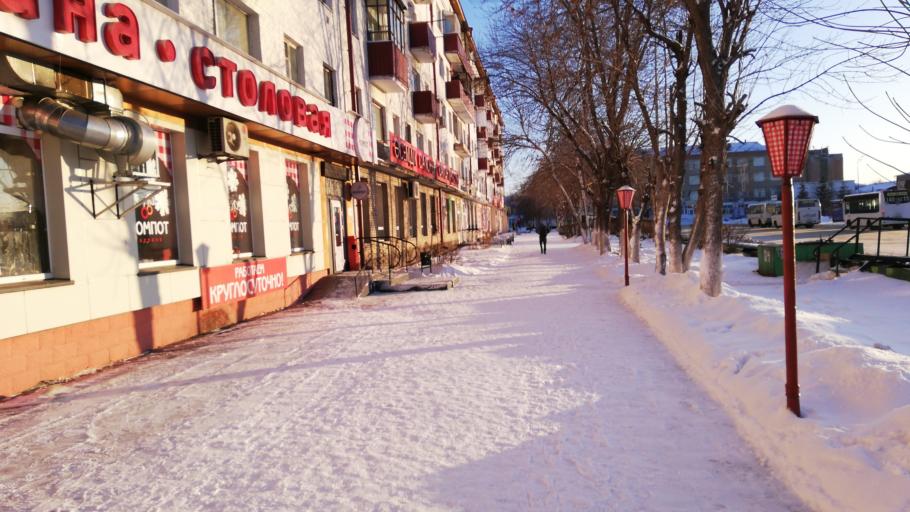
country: KZ
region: Soltustik Qazaqstan
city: Petropavlovsk
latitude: 54.8579
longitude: 69.1693
